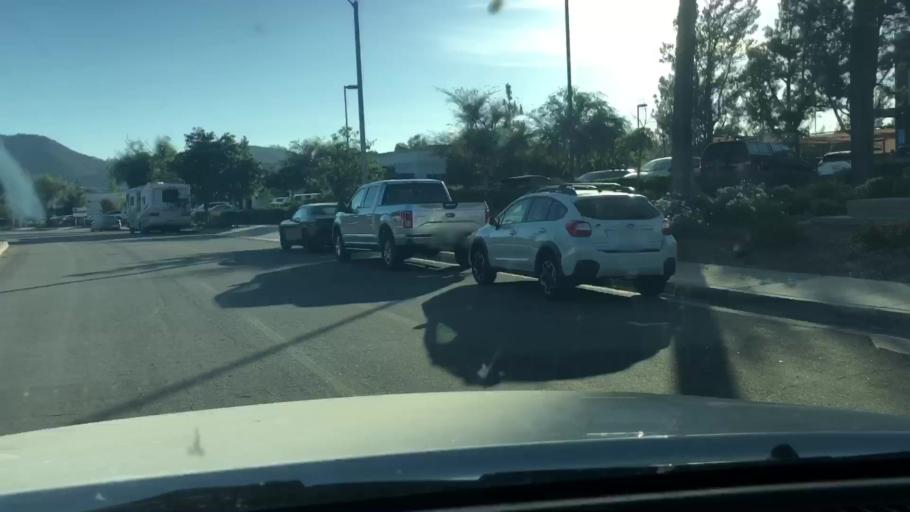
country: US
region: California
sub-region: Riverside County
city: Murrieta Hot Springs
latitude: 33.5296
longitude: -117.1756
